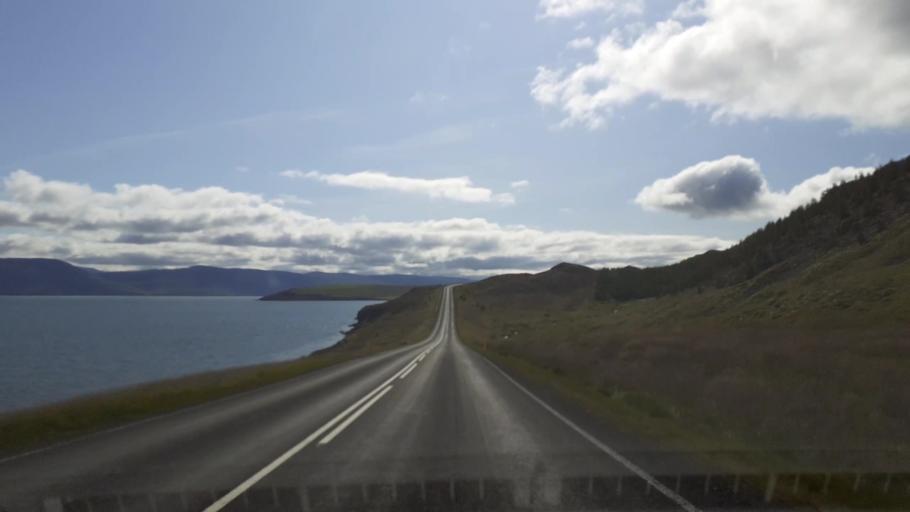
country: IS
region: Northeast
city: Dalvik
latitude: 65.8877
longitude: -18.2731
